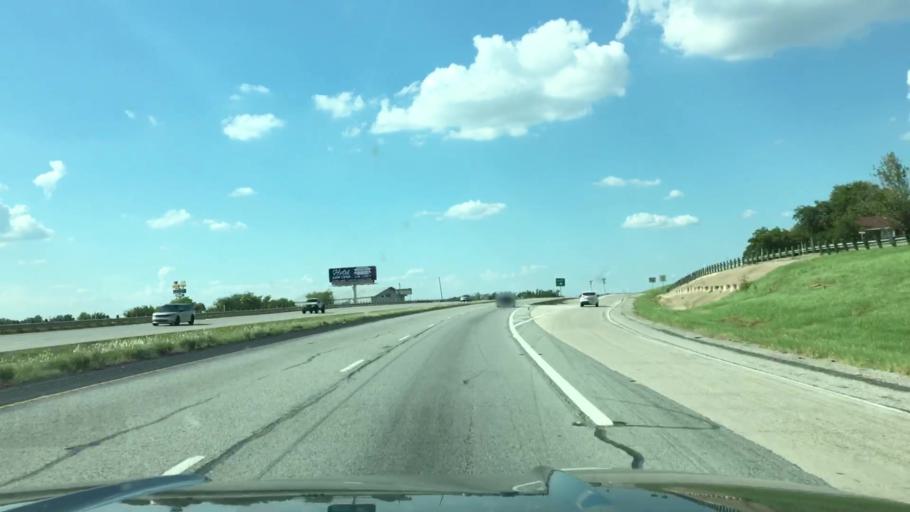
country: US
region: Texas
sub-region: Wise County
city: Rhome
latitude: 33.0505
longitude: -97.4778
